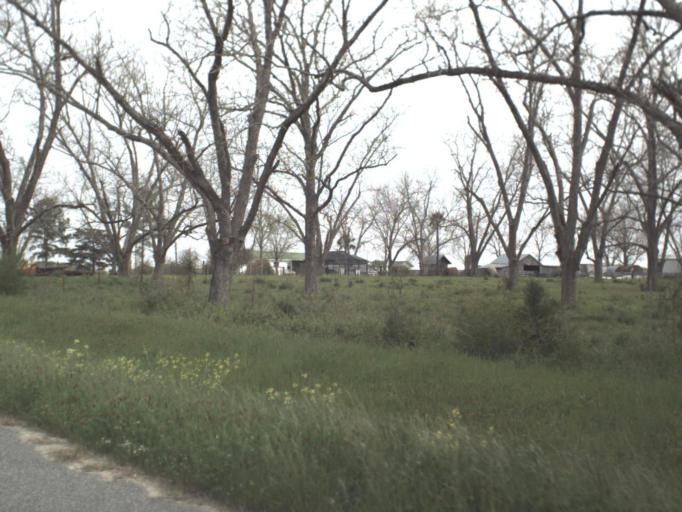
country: US
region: Florida
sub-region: Holmes County
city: Bonifay
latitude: 30.9186
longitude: -85.6492
